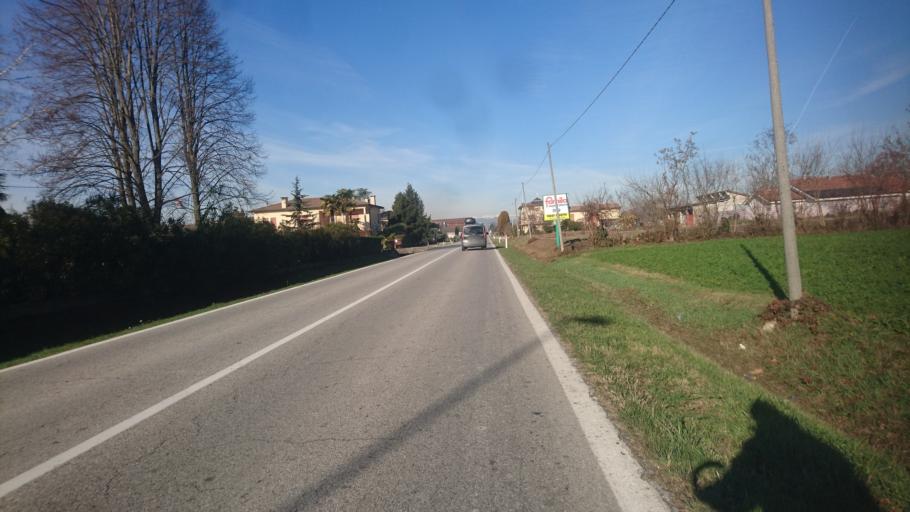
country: IT
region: Veneto
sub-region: Provincia di Padova
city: Villafranca Padovana
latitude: 45.5001
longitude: 11.7946
